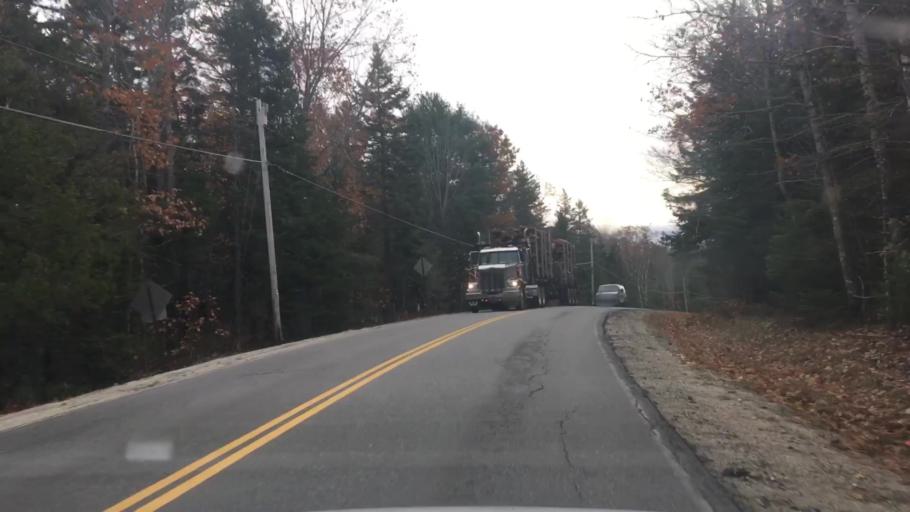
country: US
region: Maine
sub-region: Hancock County
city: Penobscot
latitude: 44.4304
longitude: -68.6270
